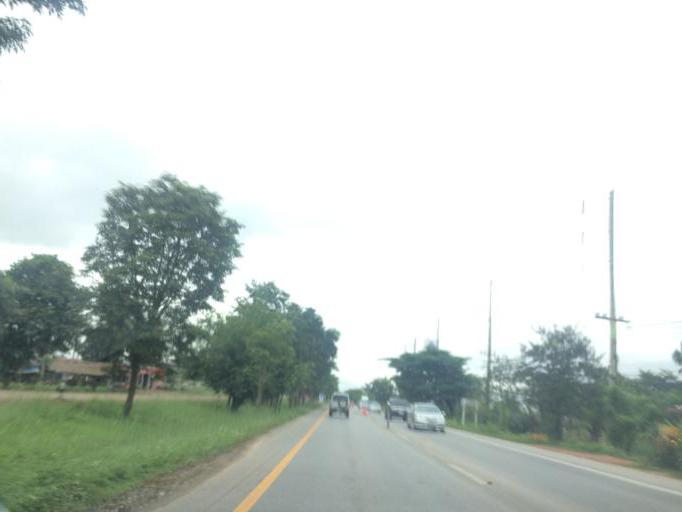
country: TH
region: Chiang Rai
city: Mae Lao
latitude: 19.7512
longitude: 99.7299
